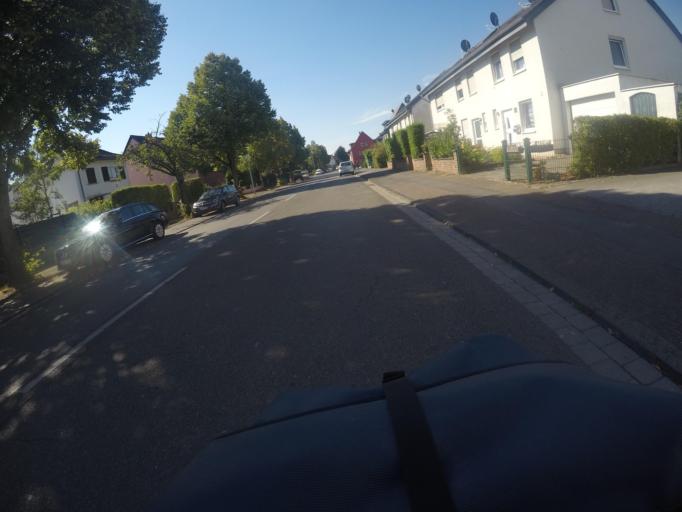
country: DE
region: North Rhine-Westphalia
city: Opladen
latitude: 51.0775
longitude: 6.9947
